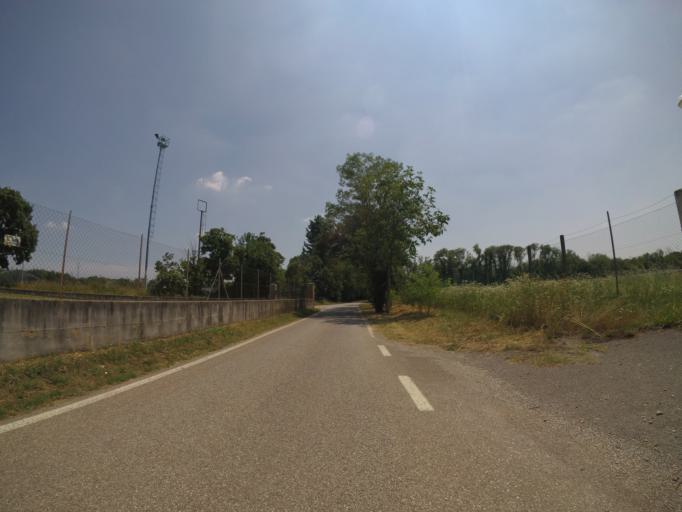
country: IT
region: Friuli Venezia Giulia
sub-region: Provincia di Udine
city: Codroipo
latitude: 45.9678
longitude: 13.0011
